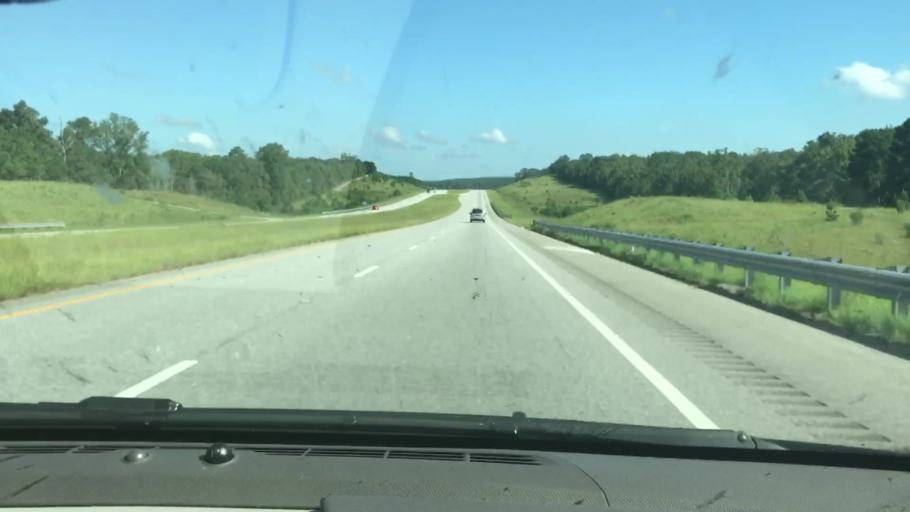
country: US
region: Alabama
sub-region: Barbour County
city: Eufaula
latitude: 32.1003
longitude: -85.1500
